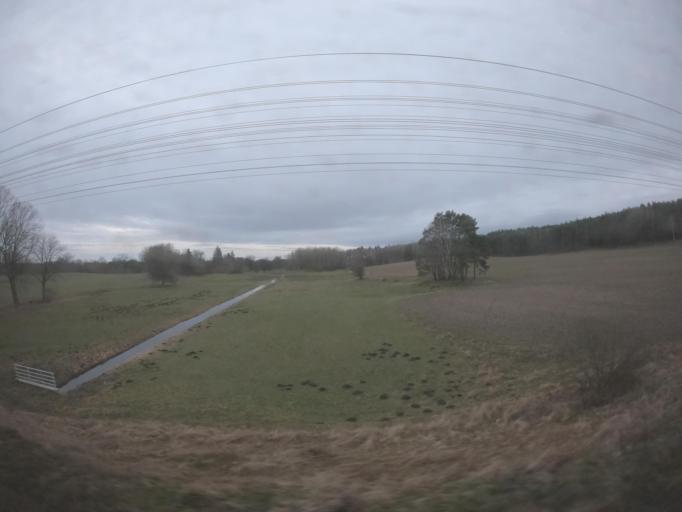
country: PL
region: West Pomeranian Voivodeship
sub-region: Powiat szczecinecki
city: Borne Sulinowo
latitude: 53.6588
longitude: 16.5473
